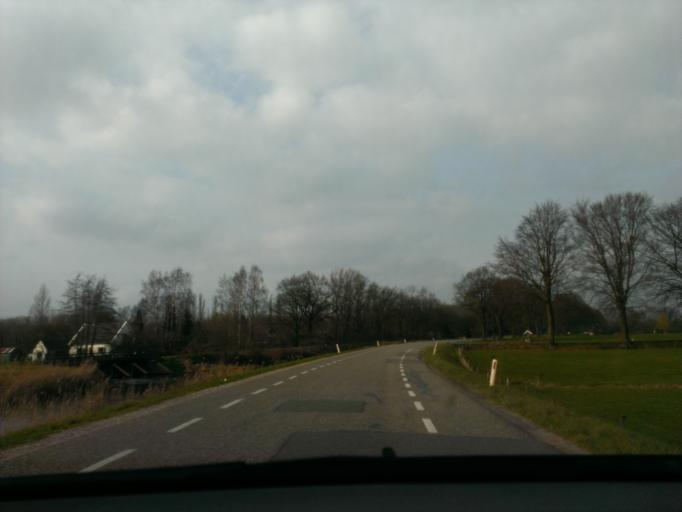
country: NL
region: Gelderland
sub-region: Gemeente Epe
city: Emst
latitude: 52.2995
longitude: 5.9998
